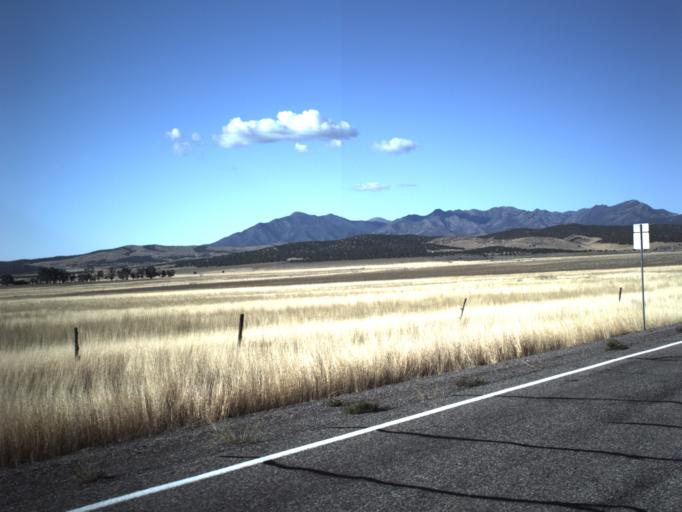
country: US
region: Utah
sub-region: Millard County
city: Fillmore
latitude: 39.1293
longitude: -112.2514
